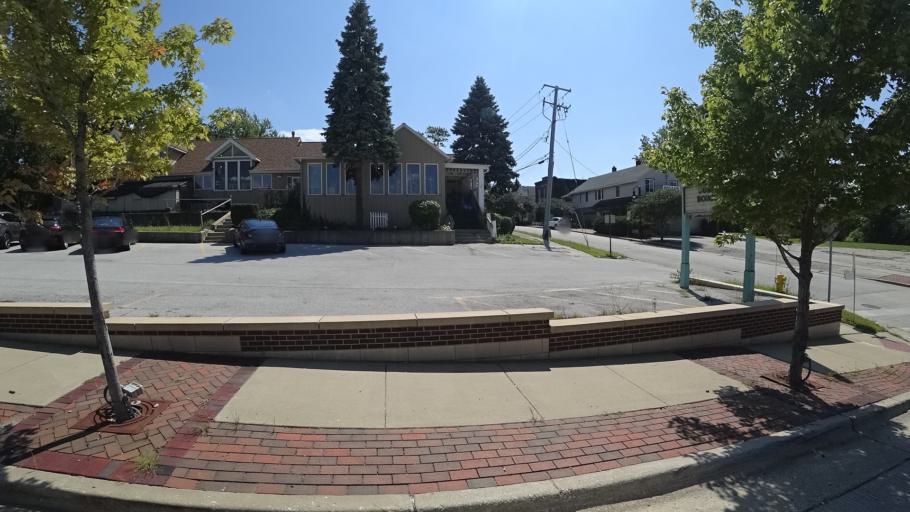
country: US
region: Illinois
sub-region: Cook County
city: Orland Park
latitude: 41.6303
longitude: -87.8590
